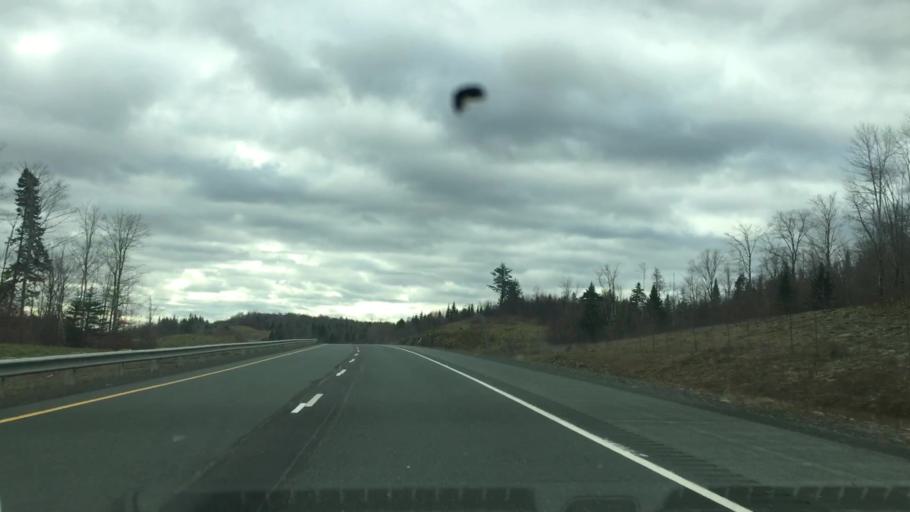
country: US
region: Maine
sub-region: Aroostook County
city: Fort Fairfield
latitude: 46.6434
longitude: -67.7443
